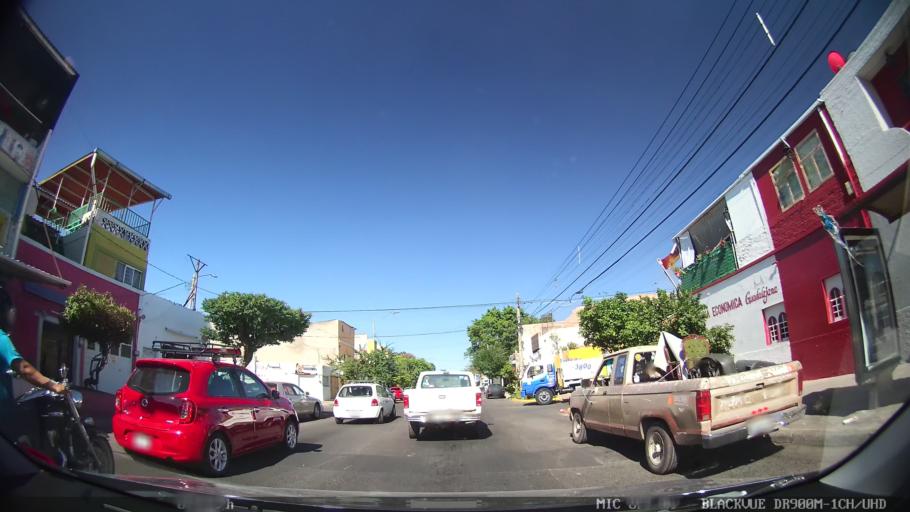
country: MX
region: Jalisco
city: Tlaquepaque
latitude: 20.6738
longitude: -103.2895
